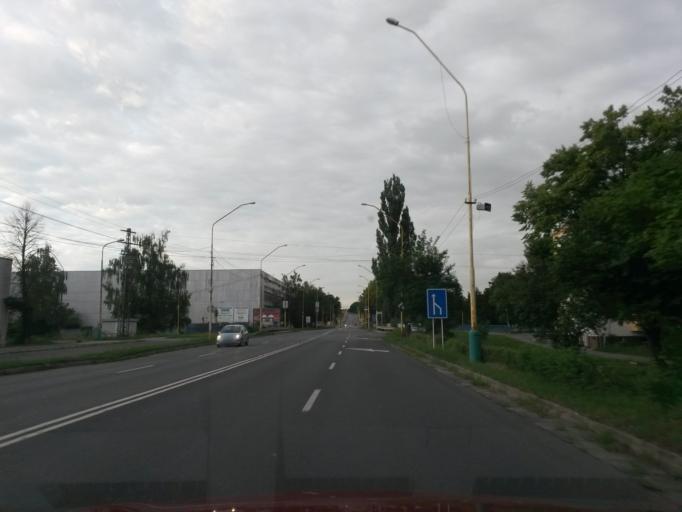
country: SK
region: Banskobystricky
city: Lucenec
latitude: 48.3359
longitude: 19.6758
